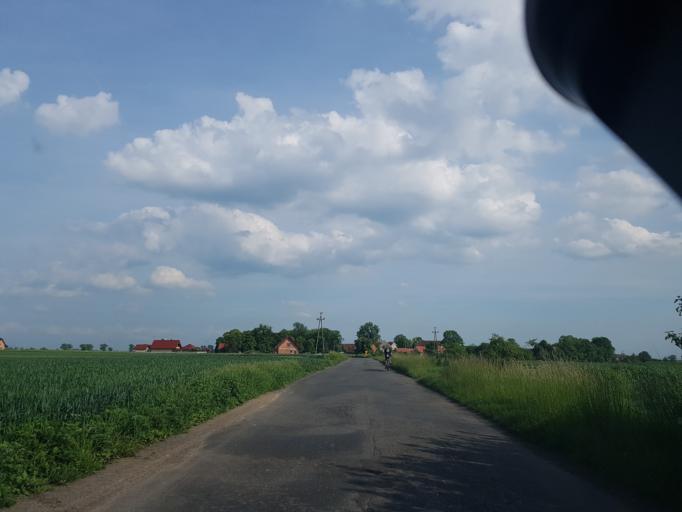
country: PL
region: Lower Silesian Voivodeship
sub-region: Powiat olawski
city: Wierzbno
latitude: 50.8719
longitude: 17.1531
